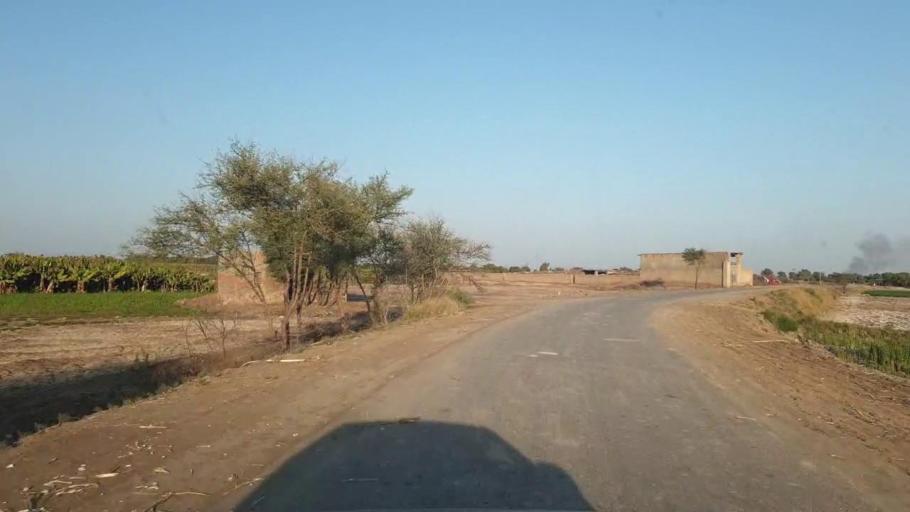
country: PK
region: Sindh
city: Tando Allahyar
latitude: 25.3542
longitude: 68.7143
